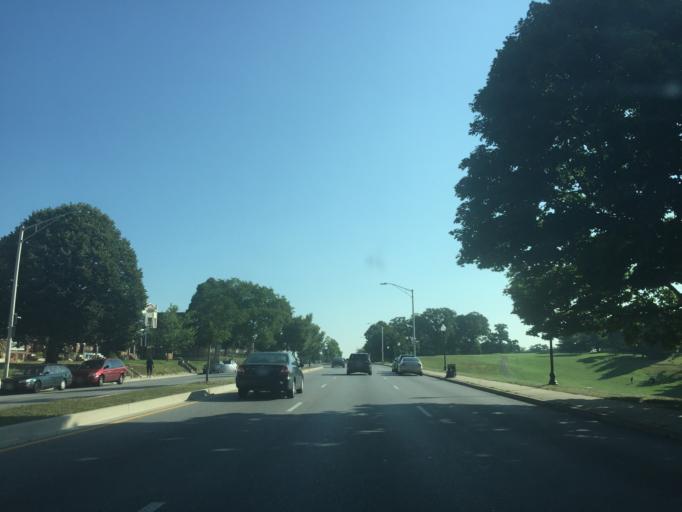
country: US
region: Maryland
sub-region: City of Baltimore
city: Baltimore
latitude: 39.3243
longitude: -76.5867
